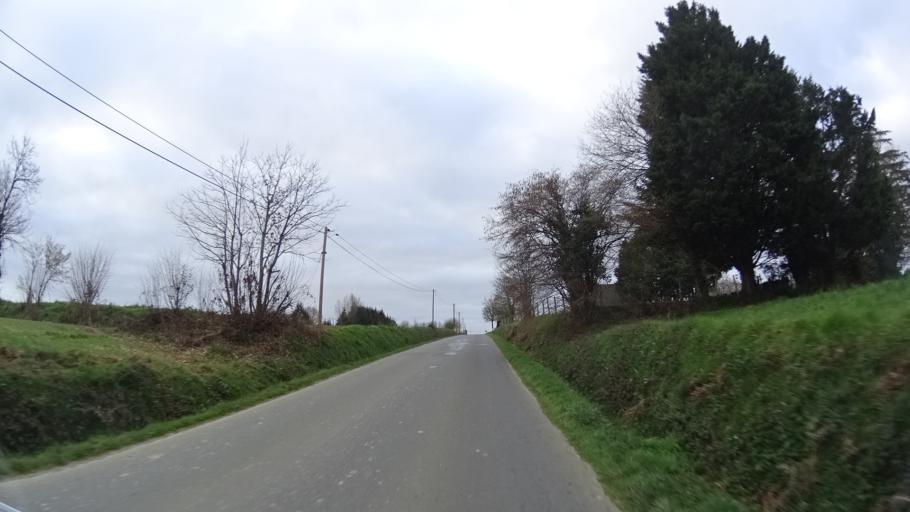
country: FR
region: Brittany
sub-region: Departement d'Ille-et-Vilaine
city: Saint-Gilles
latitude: 48.1873
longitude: -1.8337
